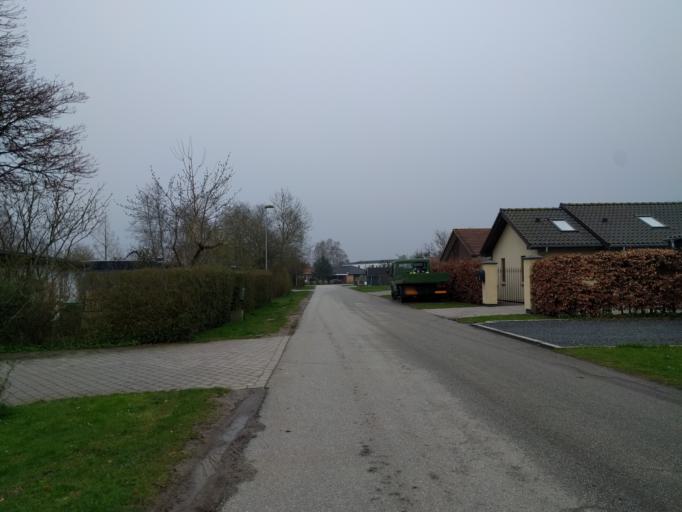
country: DK
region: Central Jutland
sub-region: Arhus Kommune
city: Lystrup
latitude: 56.2067
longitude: 10.2401
